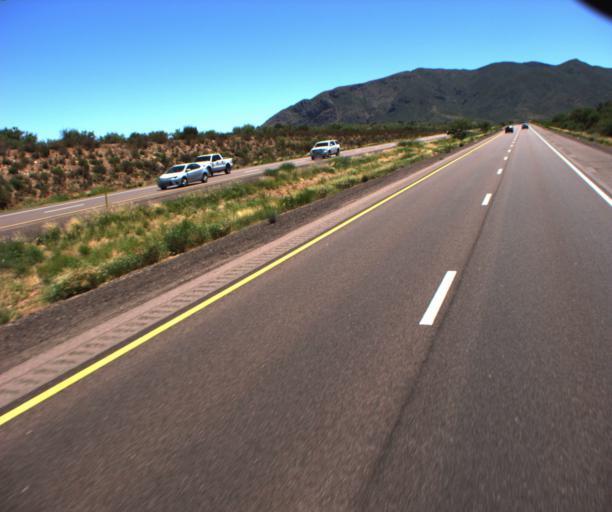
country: US
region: Arizona
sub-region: Gila County
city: Payson
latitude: 34.0532
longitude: -111.3658
